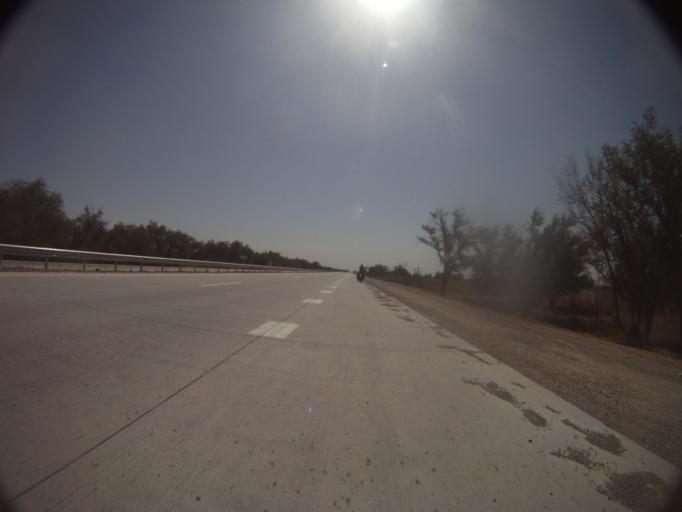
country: KZ
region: Ongtustik Qazaqstan
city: Bayaldyr
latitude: 43.0985
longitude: 68.6305
